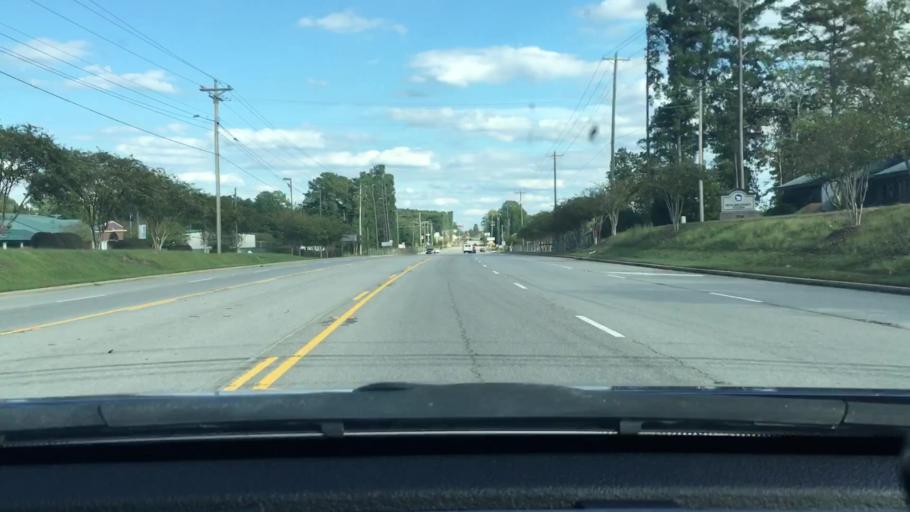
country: US
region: South Carolina
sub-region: Lexington County
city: Irmo
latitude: 34.0987
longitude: -81.1709
